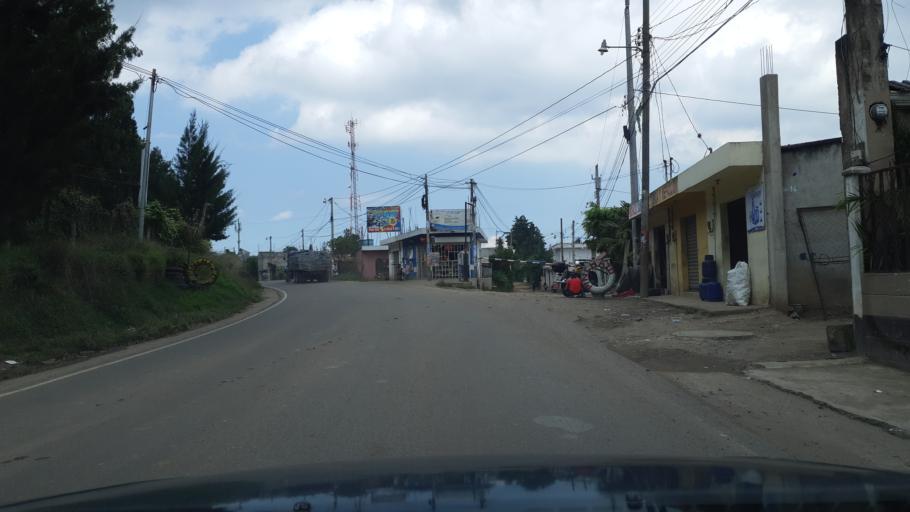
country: GT
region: Chimaltenango
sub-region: Municipio de Chimaltenango
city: Chimaltenango
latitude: 14.6862
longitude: -90.7955
